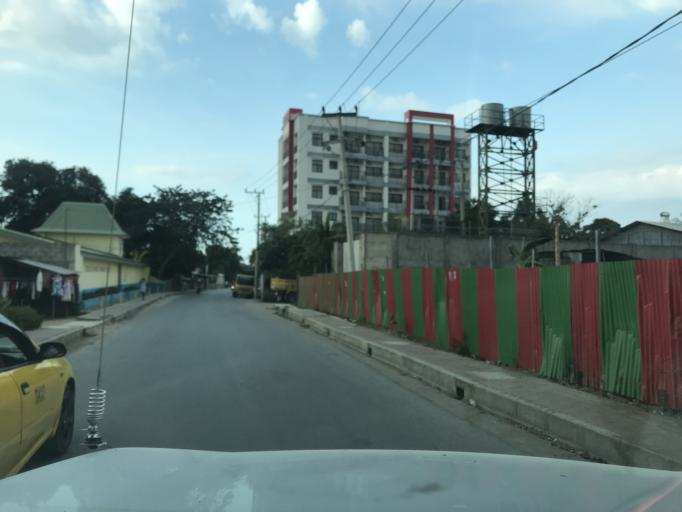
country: TL
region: Dili
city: Dili
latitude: -8.5535
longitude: 125.5398
